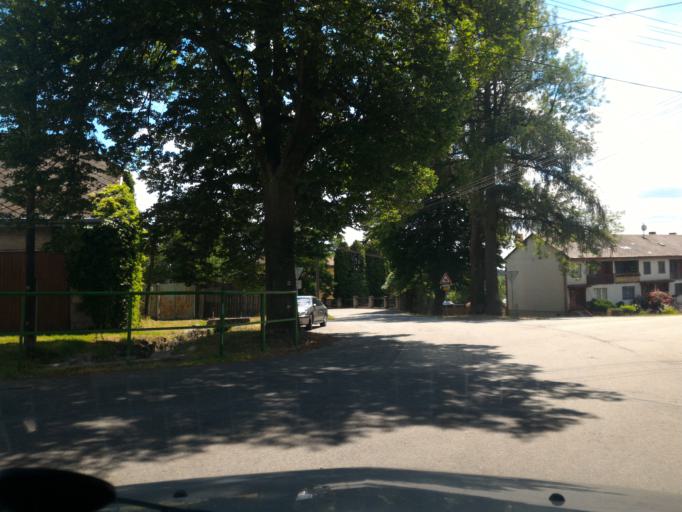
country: CZ
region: Vysocina
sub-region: Okres Jihlava
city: Telc
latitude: 49.2196
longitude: 15.3949
